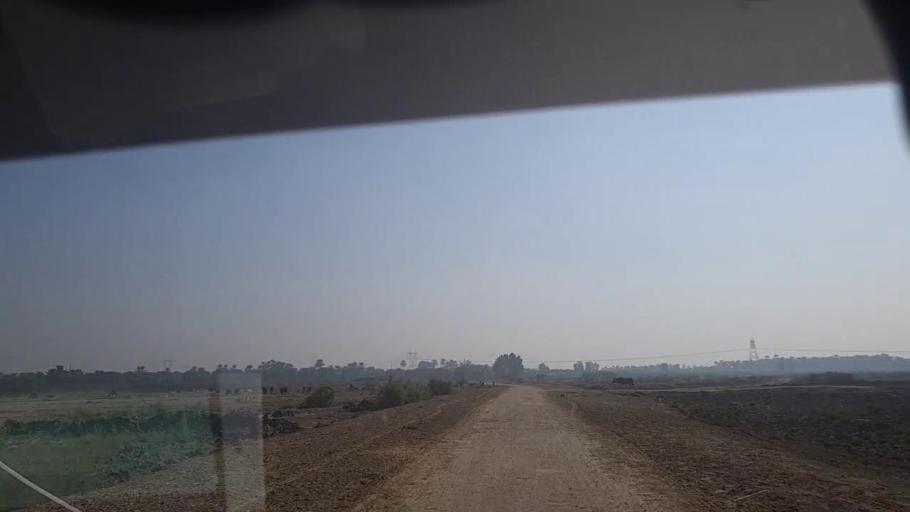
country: PK
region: Sindh
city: Khairpur
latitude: 27.4608
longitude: 68.7376
